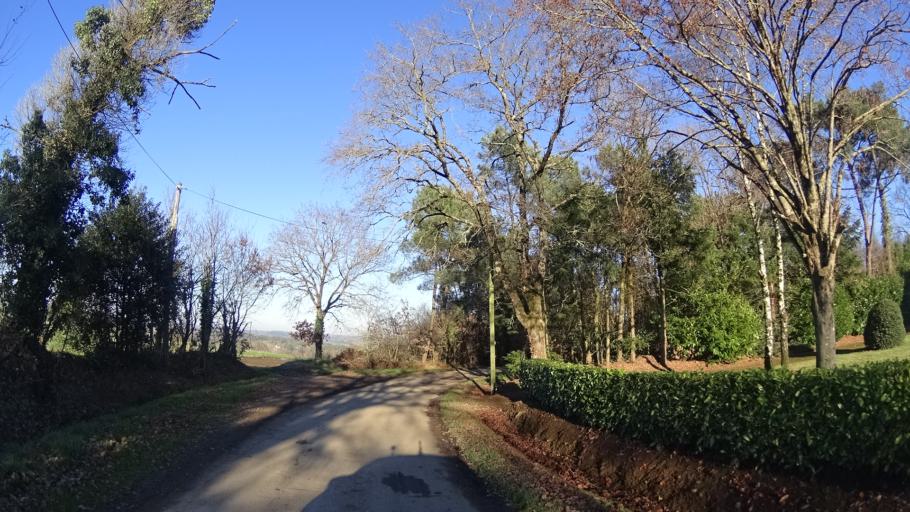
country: FR
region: Brittany
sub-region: Departement du Morbihan
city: Saint-Jacut-les-Pins
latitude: 47.6746
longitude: -2.1979
